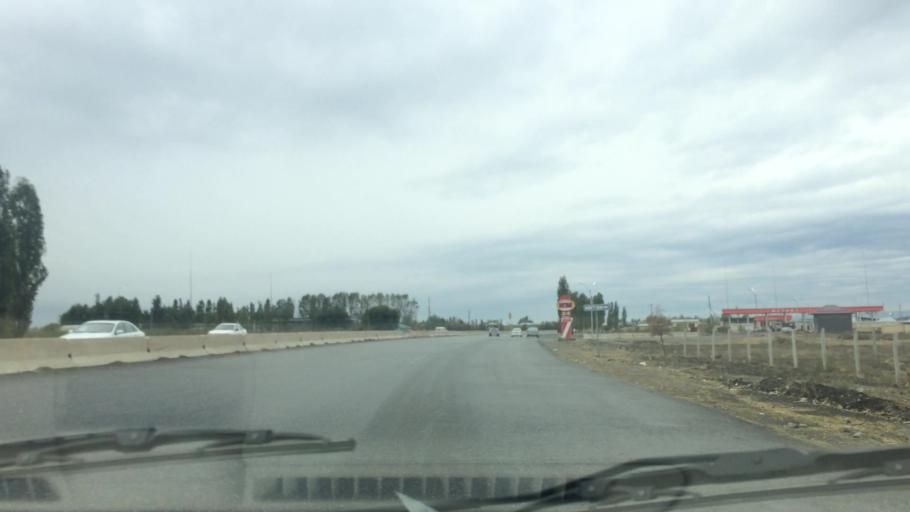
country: UZ
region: Jizzax
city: Jizzax
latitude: 40.0238
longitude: 67.6155
